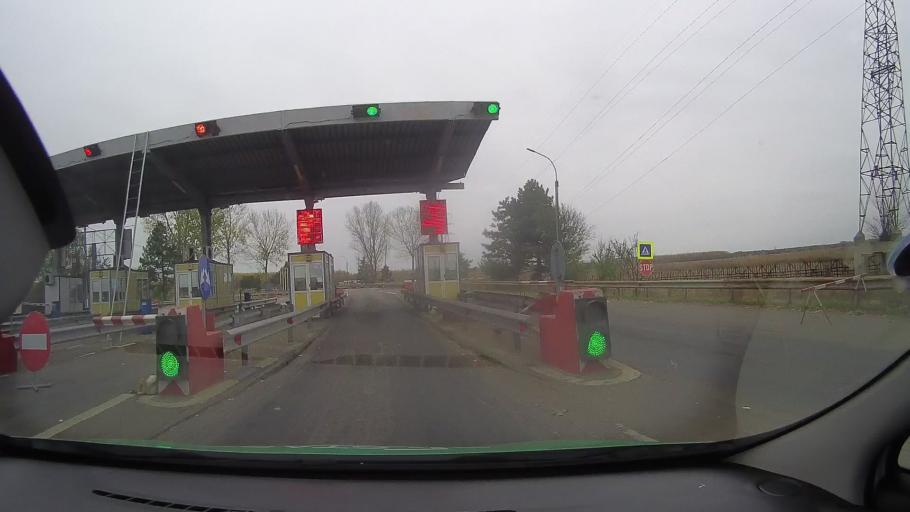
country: RO
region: Ialomita
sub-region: Comuna Giurgeni
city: Giurgeni
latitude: 44.7494
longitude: 27.8929
